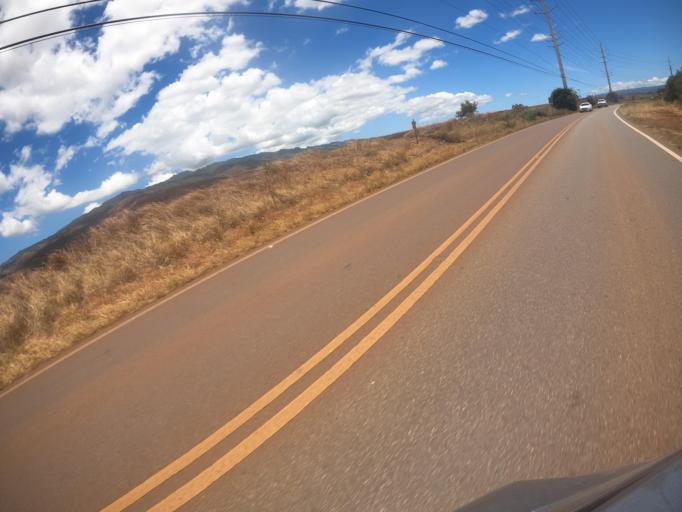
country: US
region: Hawaii
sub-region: Honolulu County
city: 'Ewa Villages
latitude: 21.3658
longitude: -158.0530
